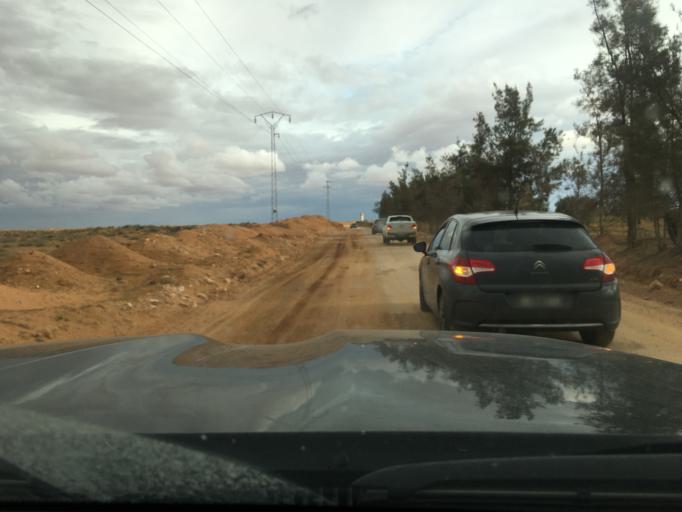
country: TN
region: Madanin
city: Medenine
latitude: 33.2740
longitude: 10.5639
